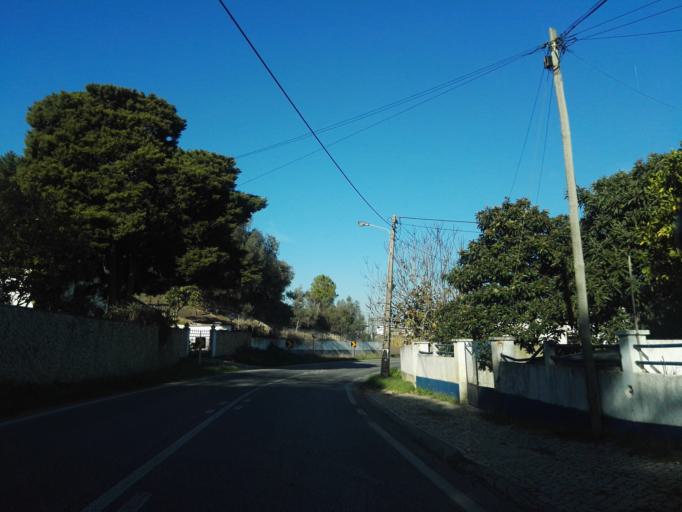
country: PT
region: Lisbon
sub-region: Alenquer
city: Carregado
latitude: 39.0139
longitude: -8.9828
